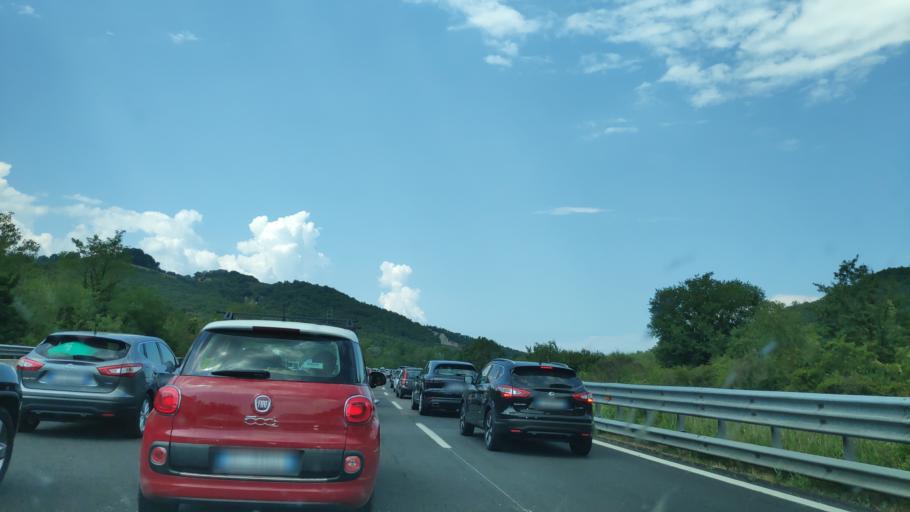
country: IT
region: Umbria
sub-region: Provincia di Terni
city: Stazione di Allerona
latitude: 42.8060
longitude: 12.0384
